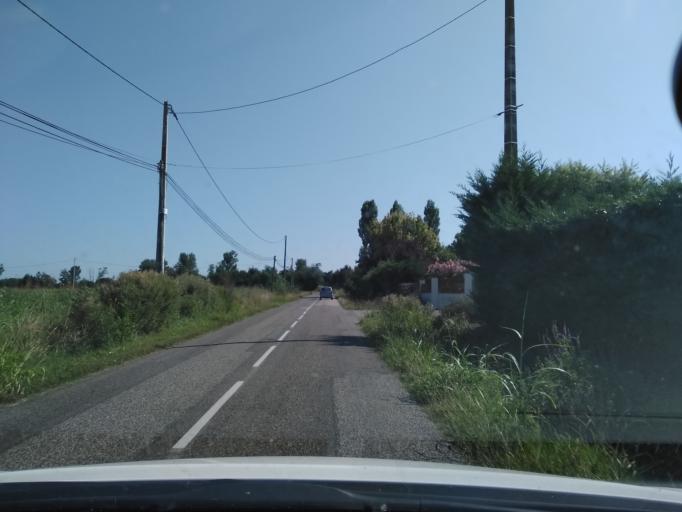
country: FR
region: Midi-Pyrenees
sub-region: Departement du Tarn-et-Garonne
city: Montech
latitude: 43.9686
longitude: 1.2411
